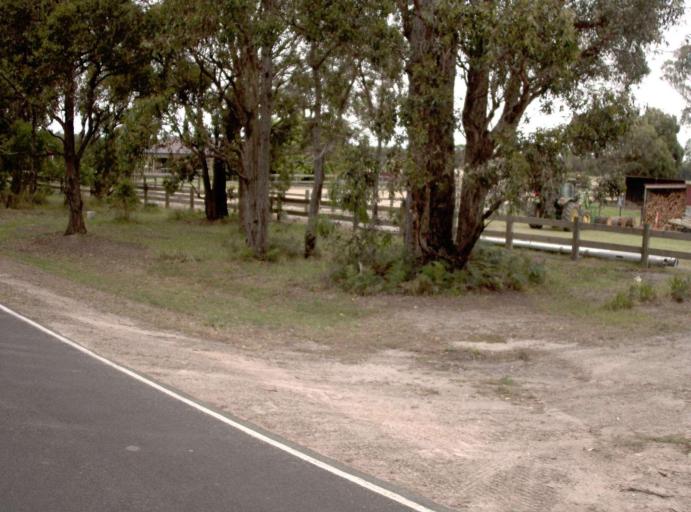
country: AU
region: Victoria
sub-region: Latrobe
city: Traralgon
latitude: -38.5185
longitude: 146.8581
